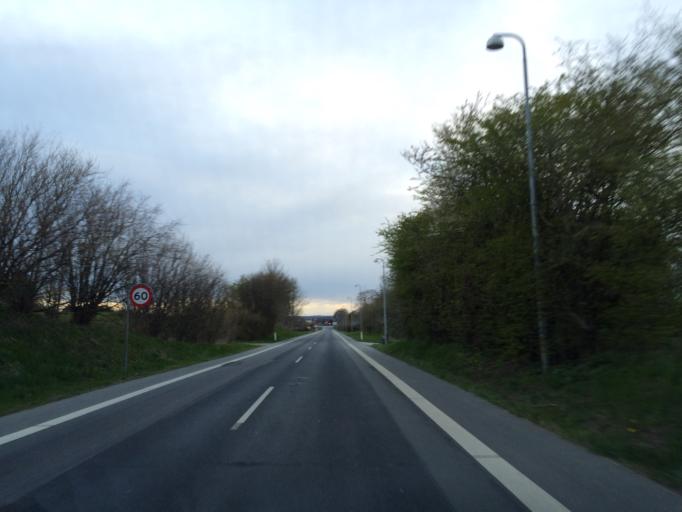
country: DK
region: South Denmark
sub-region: Odense Kommune
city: Bellinge
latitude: 55.3843
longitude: 10.2637
